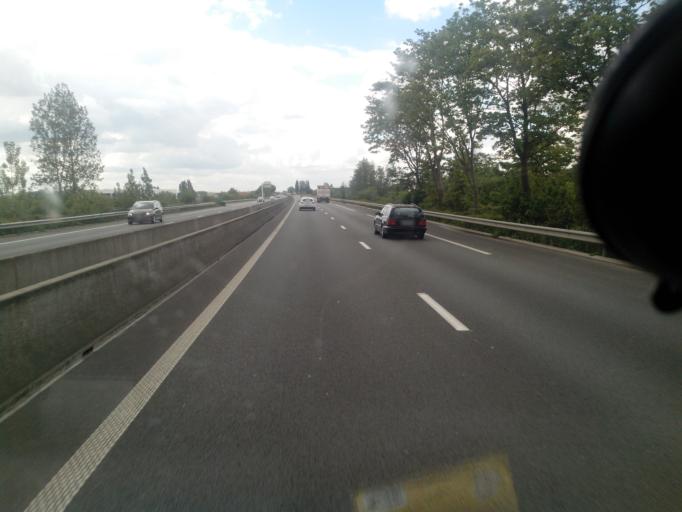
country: FR
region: Nord-Pas-de-Calais
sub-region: Departement du Nord
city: Bailleul
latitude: 50.7218
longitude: 2.7442
